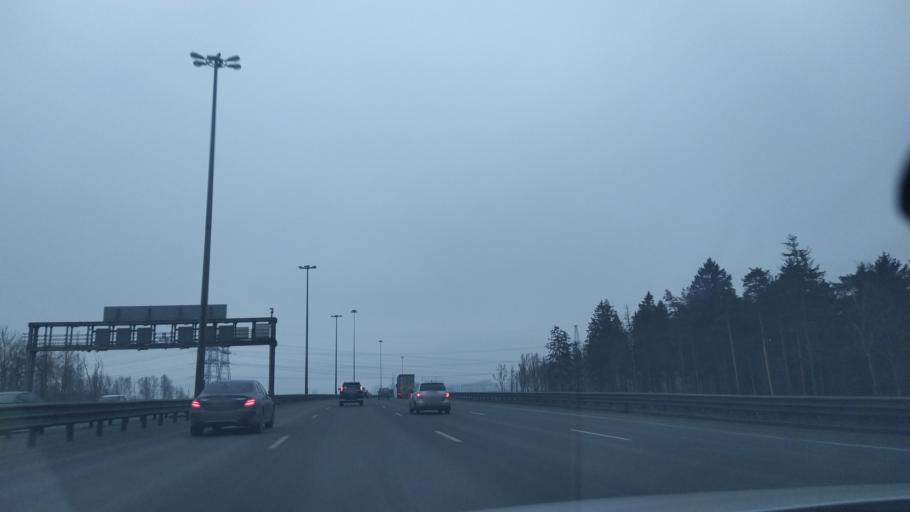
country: RU
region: St.-Petersburg
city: Krasnogvargeisky
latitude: 59.9337
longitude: 30.5376
